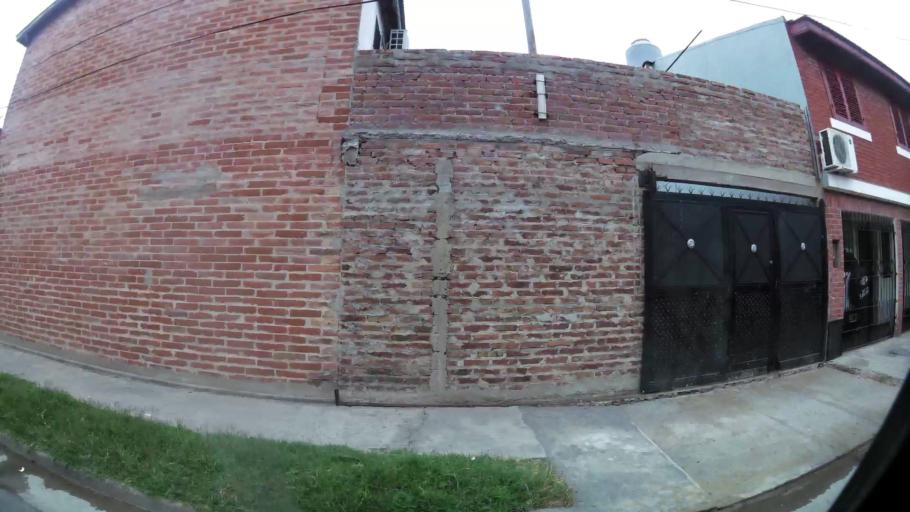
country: AR
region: Buenos Aires
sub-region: Partido de Avellaneda
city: Avellaneda
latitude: -34.6448
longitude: -58.3492
